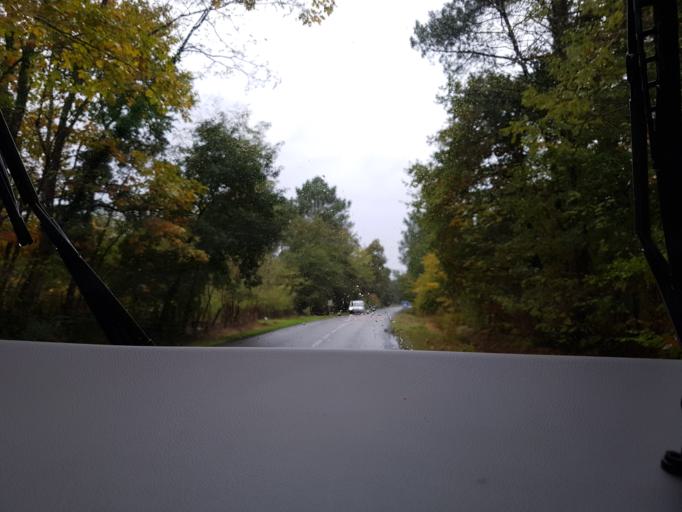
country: FR
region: Aquitaine
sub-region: Departement des Landes
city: Pissos
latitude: 44.3658
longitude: -0.6440
